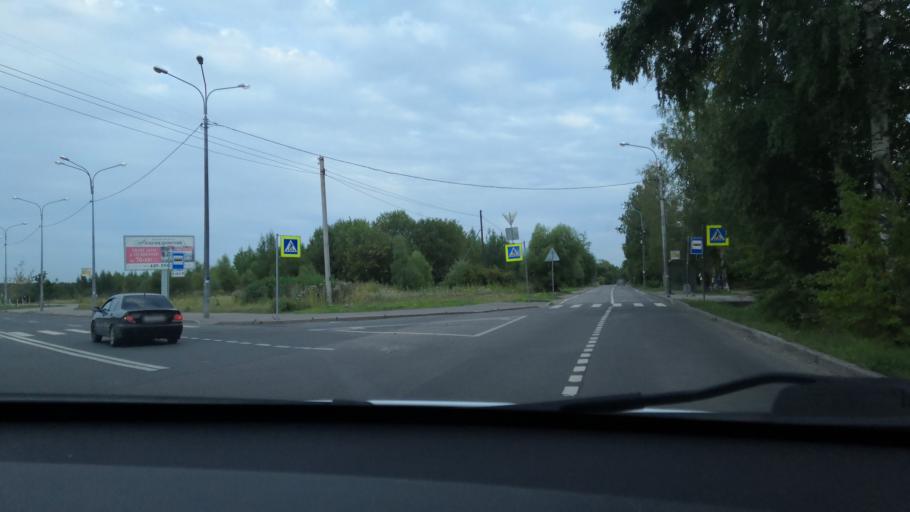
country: RU
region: St.-Petersburg
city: Pushkin
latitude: 59.6956
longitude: 30.4126
